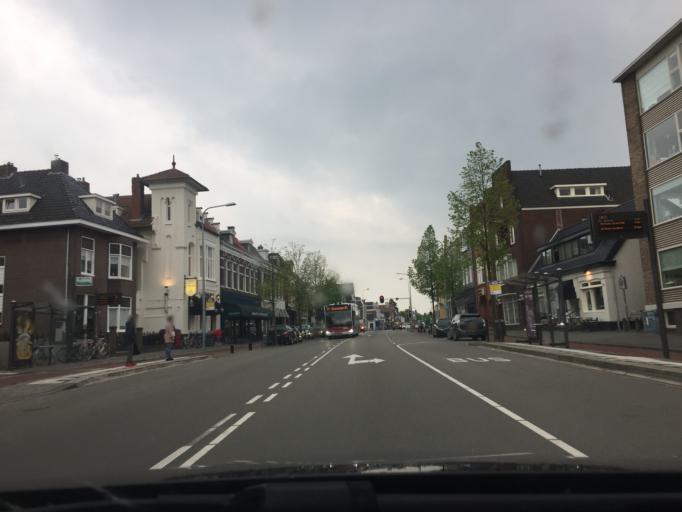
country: NL
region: Groningen
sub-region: Gemeente Groningen
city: Groningen
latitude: 53.2001
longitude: 6.5786
